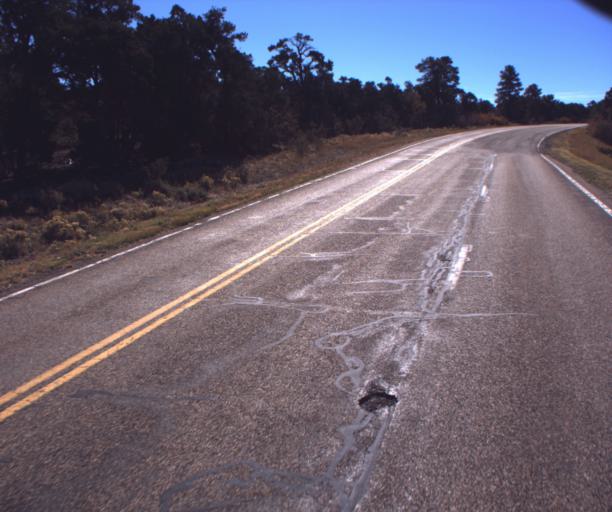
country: US
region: Arizona
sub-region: Coconino County
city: Fredonia
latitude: 36.7979
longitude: -112.2544
